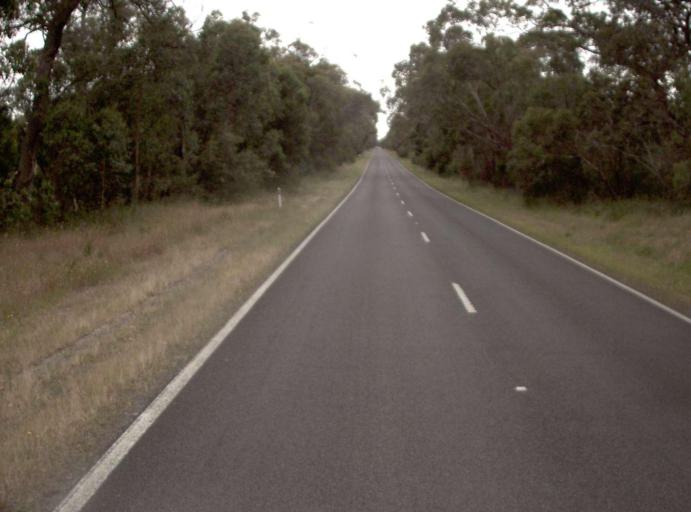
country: AU
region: Victoria
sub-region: Latrobe
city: Traralgon
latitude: -38.5373
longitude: 146.8479
